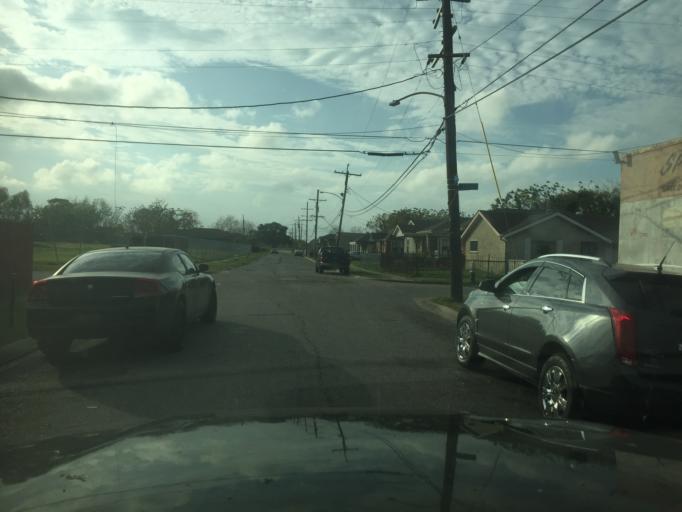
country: US
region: Louisiana
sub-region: Orleans Parish
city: New Orleans
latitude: 29.9957
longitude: -90.0792
